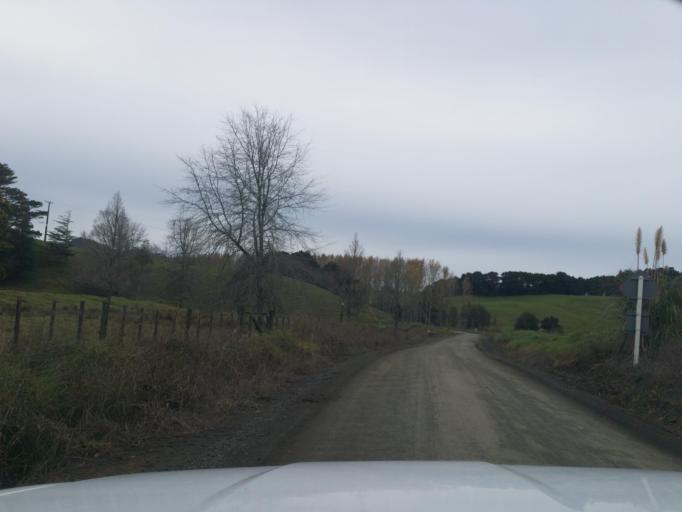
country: NZ
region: Northland
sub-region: Whangarei
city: Maungatapere
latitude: -35.8134
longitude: 174.0367
